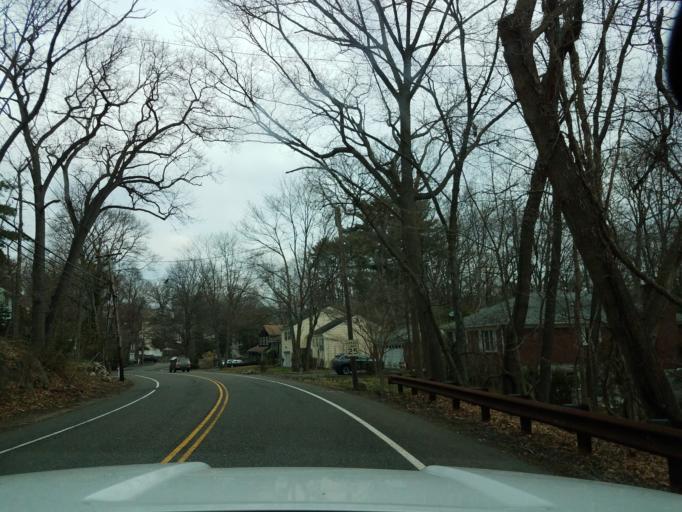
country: US
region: Connecticut
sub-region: Fairfield County
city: Riverside
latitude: 41.0414
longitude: -73.5682
